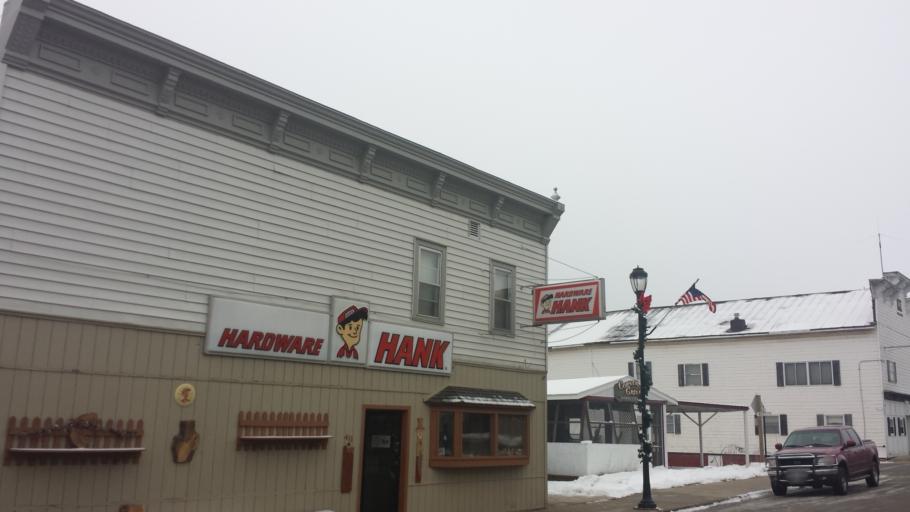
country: US
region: Wisconsin
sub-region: Monroe County
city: Tomah
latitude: 43.8130
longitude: -90.5288
